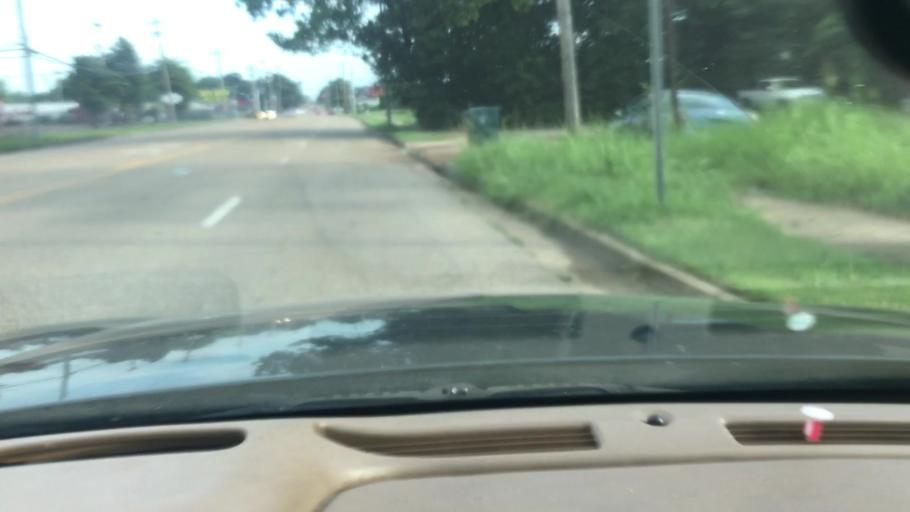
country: US
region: Tennessee
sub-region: Shelby County
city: New South Memphis
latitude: 35.0570
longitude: -90.0075
